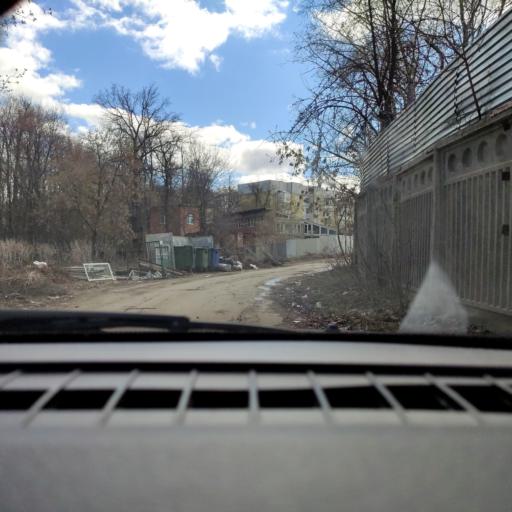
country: RU
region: Samara
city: Petra-Dubrava
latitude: 53.2878
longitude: 50.2434
